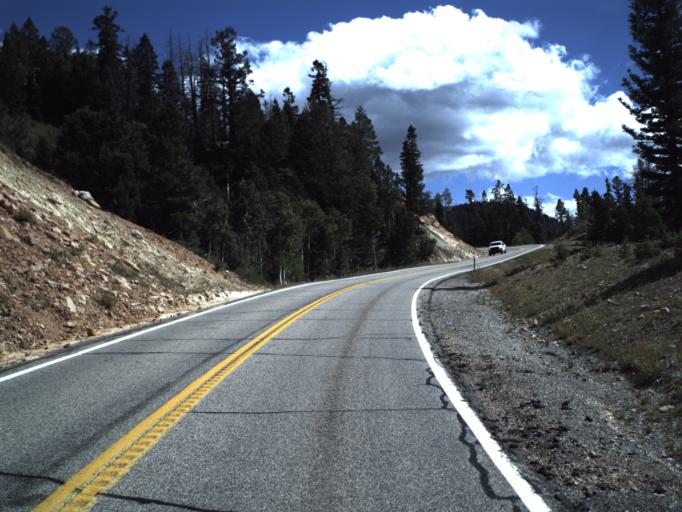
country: US
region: Utah
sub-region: Iron County
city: Cedar City
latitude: 37.5788
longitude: -112.8704
